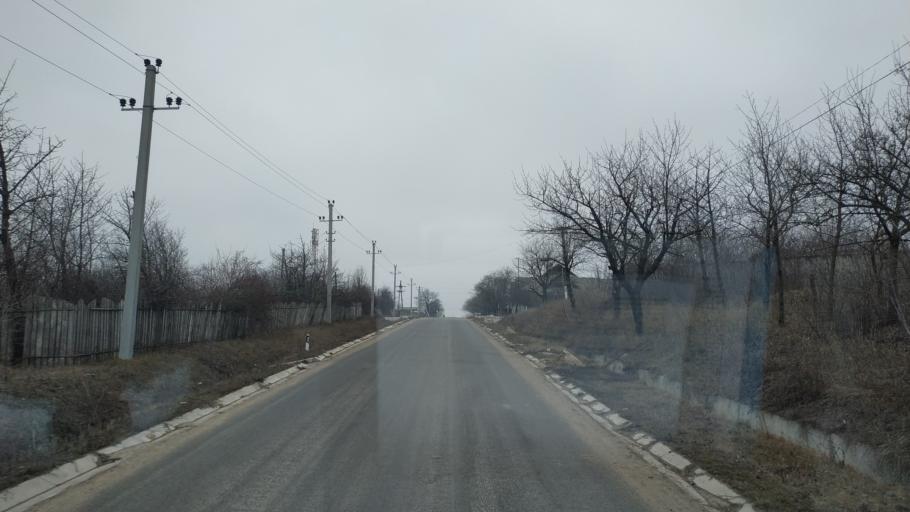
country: MD
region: Stinga Nistrului
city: Bucovat
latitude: 47.0266
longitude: 28.4207
